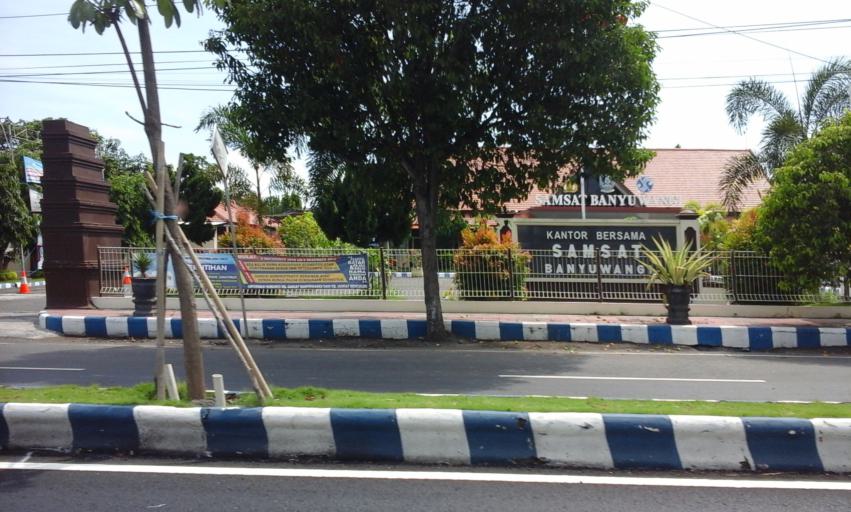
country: ID
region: East Java
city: Banyuwangi
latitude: -8.2340
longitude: 114.3550
